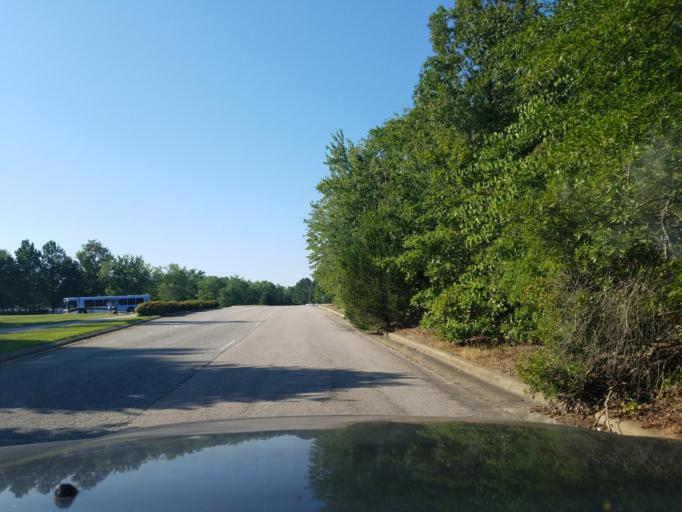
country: US
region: North Carolina
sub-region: Orange County
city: Chapel Hill
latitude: 35.8998
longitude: -79.0110
